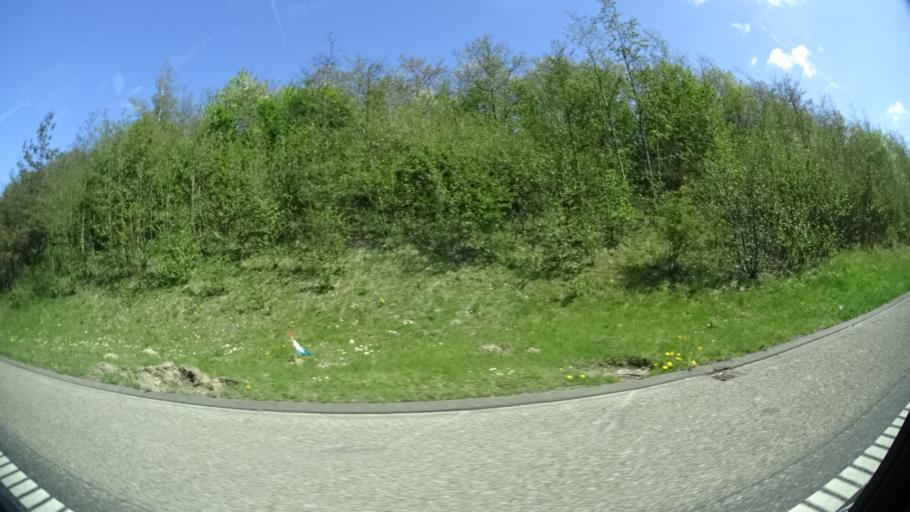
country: DK
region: Central Jutland
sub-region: Skanderborg Kommune
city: Horning
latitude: 56.1207
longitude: 10.0362
